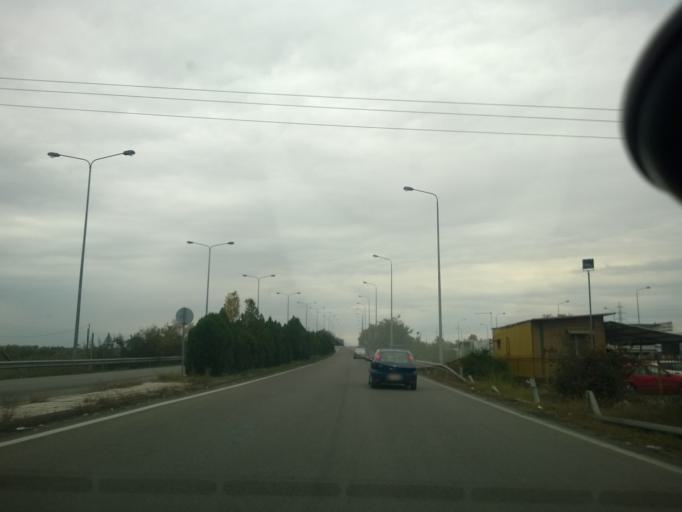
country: GR
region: Central Macedonia
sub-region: Nomos Pellis
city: Melissi
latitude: 40.7778
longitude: 22.3641
